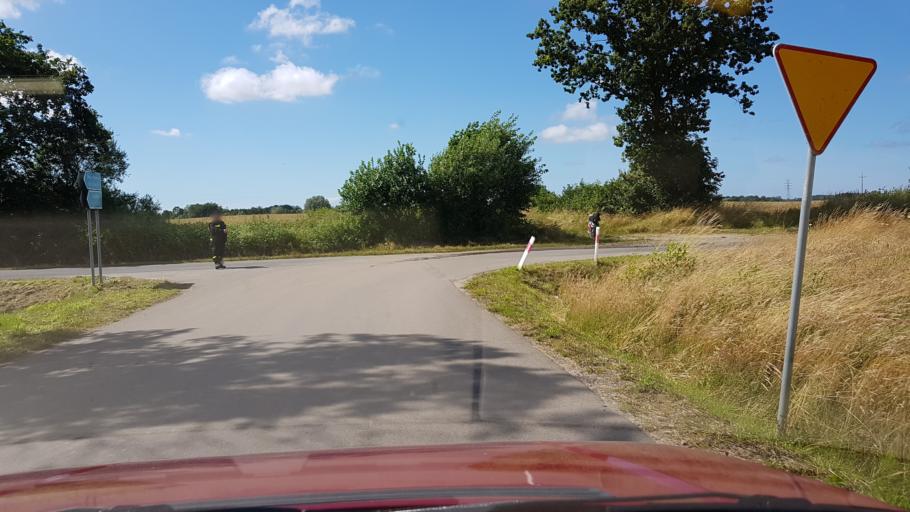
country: PL
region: West Pomeranian Voivodeship
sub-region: Powiat bialogardzki
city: Karlino
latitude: 54.1681
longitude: 15.9192
